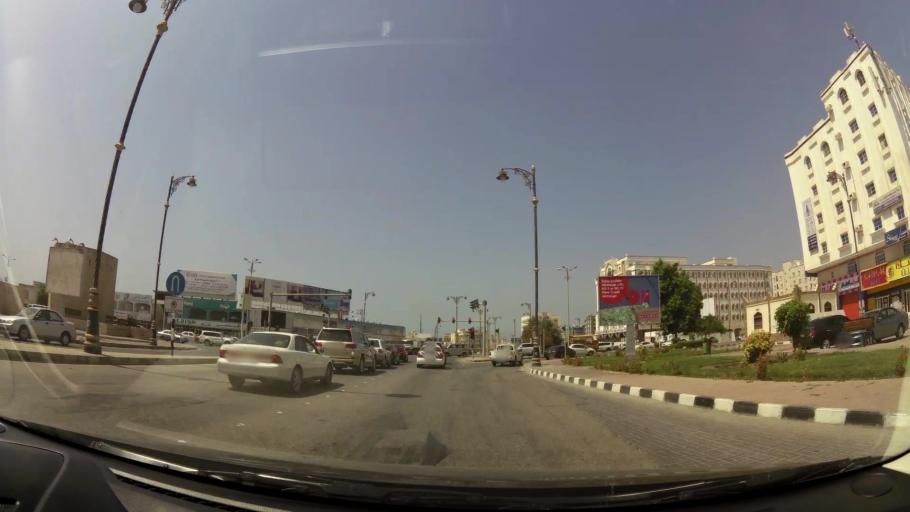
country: OM
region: Zufar
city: Salalah
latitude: 17.0199
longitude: 54.1107
